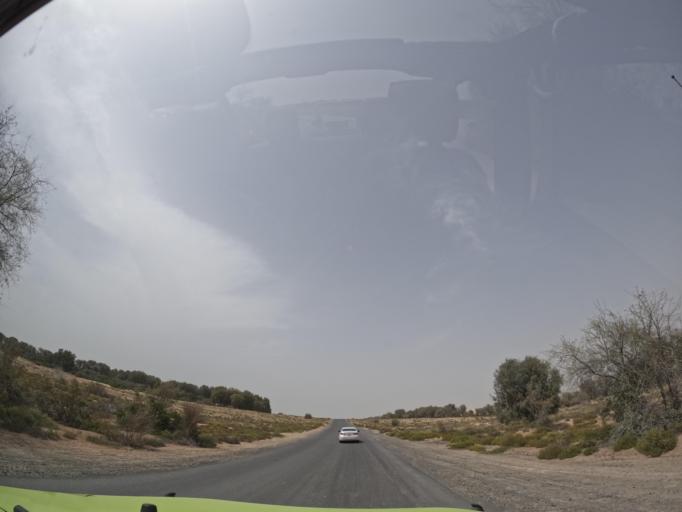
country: AE
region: Dubai
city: Dubai
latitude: 25.1415
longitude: 55.3407
